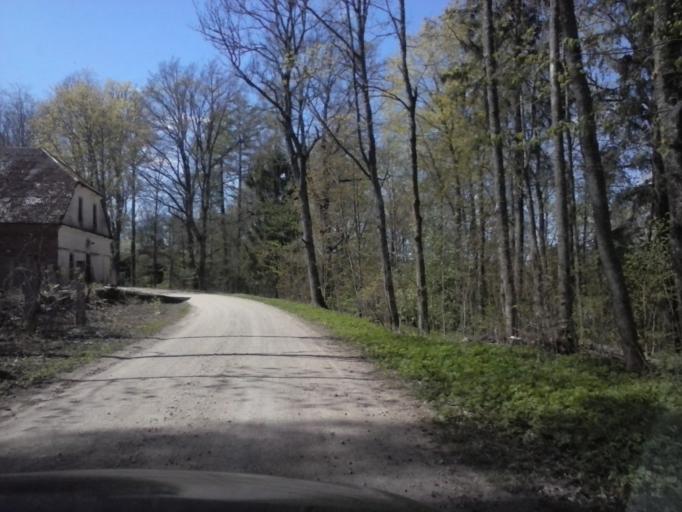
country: EE
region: Valgamaa
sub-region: Torva linn
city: Torva
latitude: 58.2341
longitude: 25.8936
